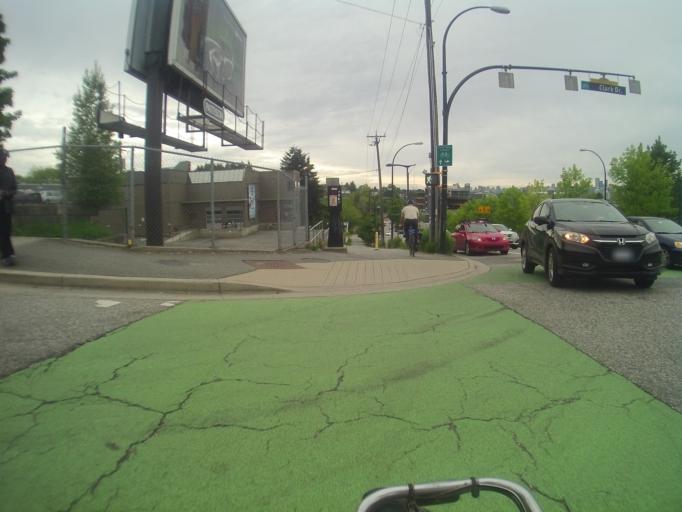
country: CA
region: British Columbia
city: Vancouver
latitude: 49.2651
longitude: -123.0774
